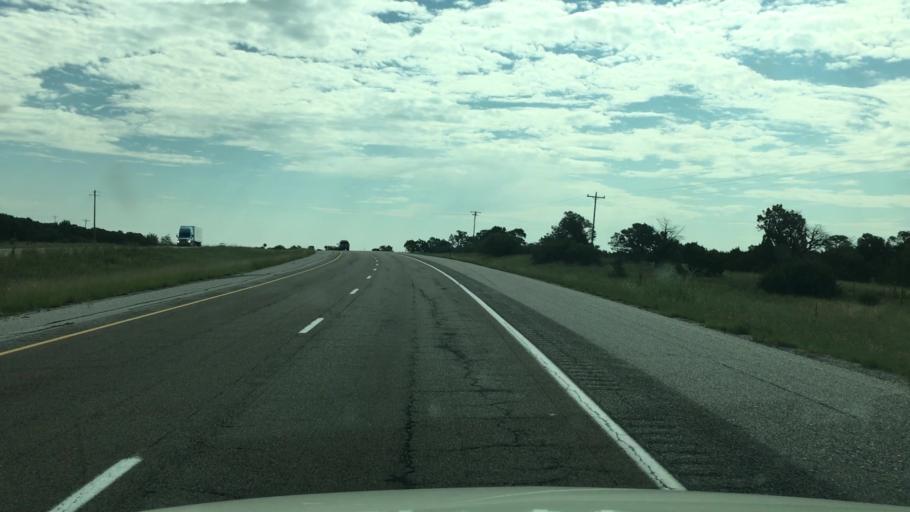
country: US
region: New Mexico
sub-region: Torrance County
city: Moriarty
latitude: 35.0019
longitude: -105.5526
